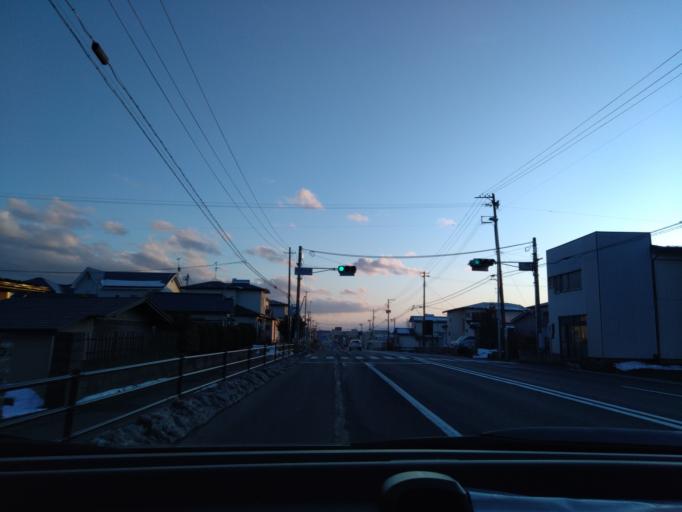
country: JP
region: Iwate
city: Hanamaki
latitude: 39.4217
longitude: 141.1290
